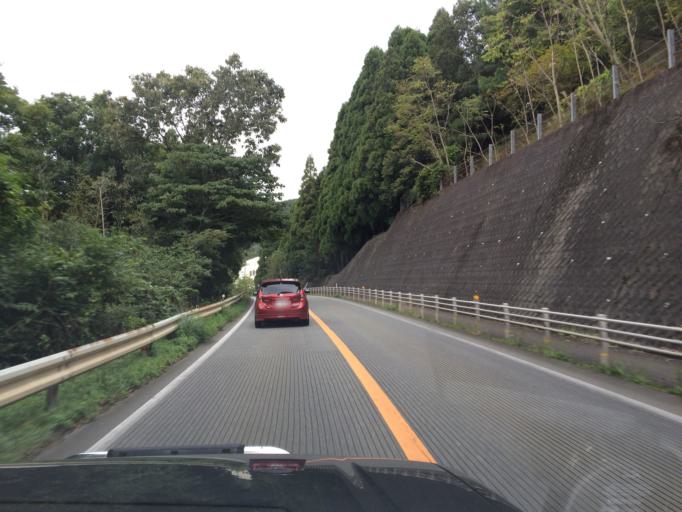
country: JP
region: Hyogo
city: Toyooka
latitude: 35.3642
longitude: 134.8257
